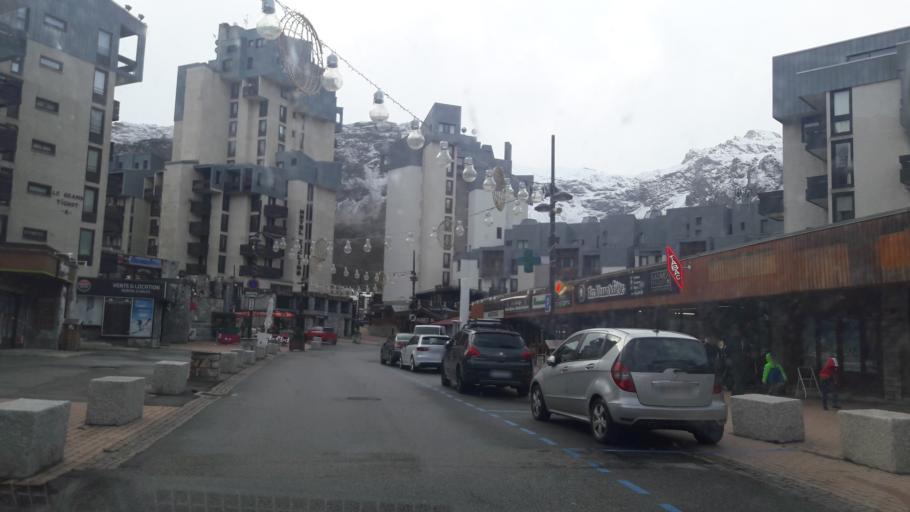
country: FR
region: Rhone-Alpes
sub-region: Departement de la Savoie
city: Tignes
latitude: 45.4574
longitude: 6.9007
